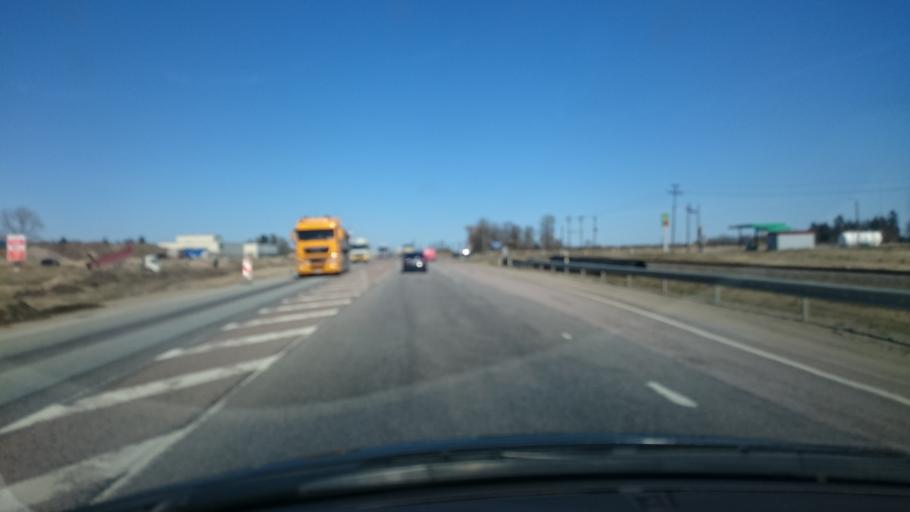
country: EE
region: Harju
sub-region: Joelaehtme vald
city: Loo
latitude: 59.4119
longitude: 24.9183
